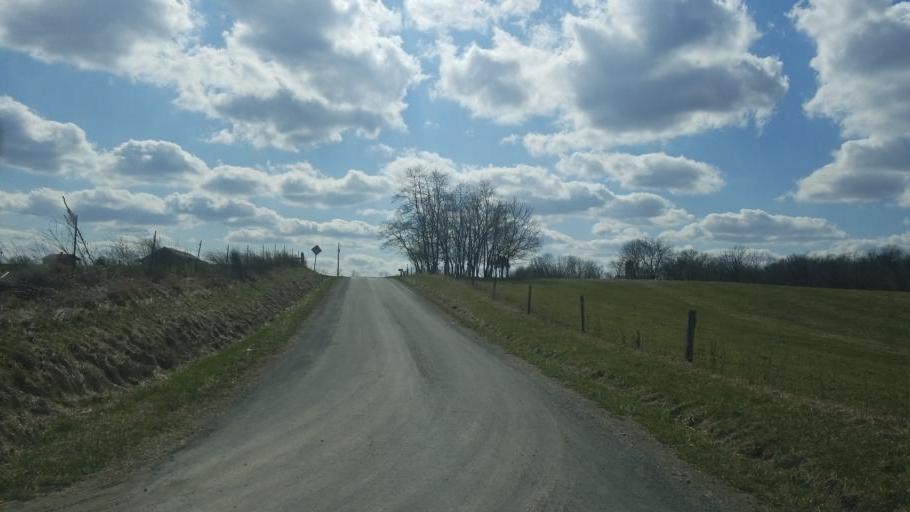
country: US
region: Ohio
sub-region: Highland County
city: Greenfield
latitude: 39.2790
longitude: -83.4373
